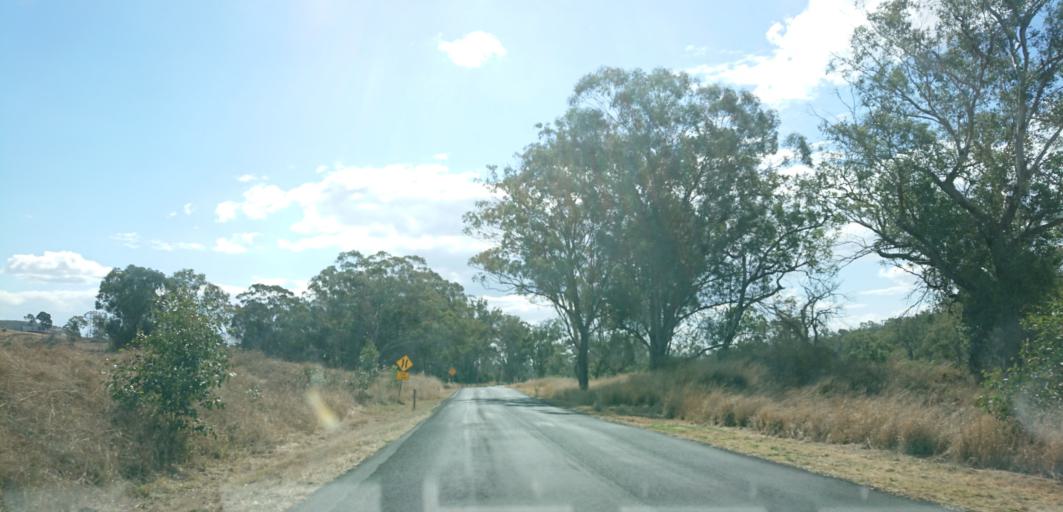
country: AU
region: Queensland
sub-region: Toowoomba
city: Top Camp
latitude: -27.8013
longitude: 152.1057
